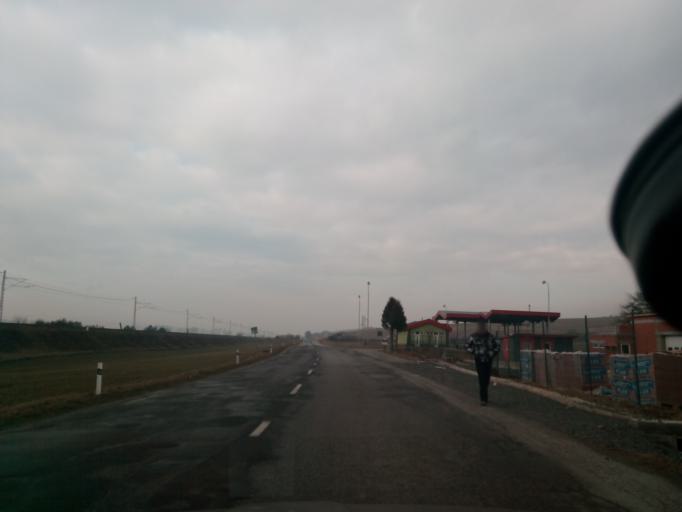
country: SK
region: Presovsky
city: Lipany
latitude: 49.1380
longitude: 21.0174
